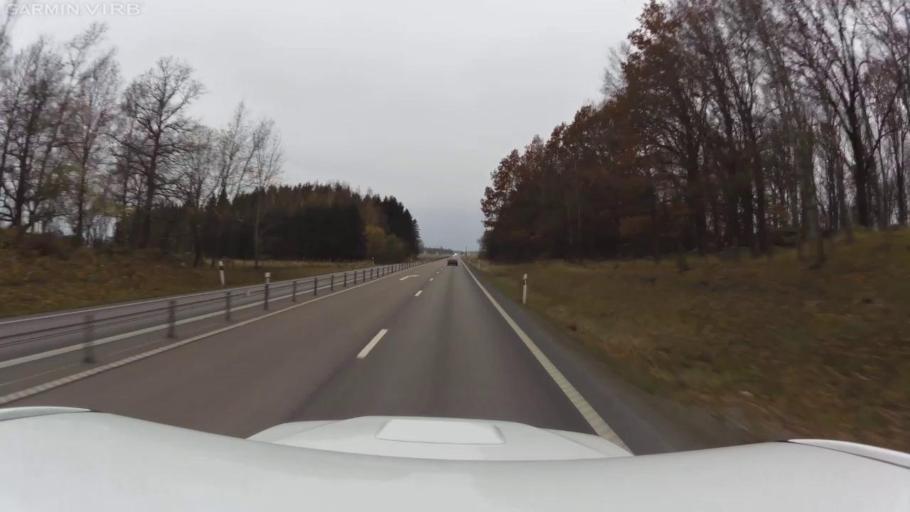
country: SE
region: OEstergoetland
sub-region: Linkopings Kommun
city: Vikingstad
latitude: 58.3747
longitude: 15.4804
